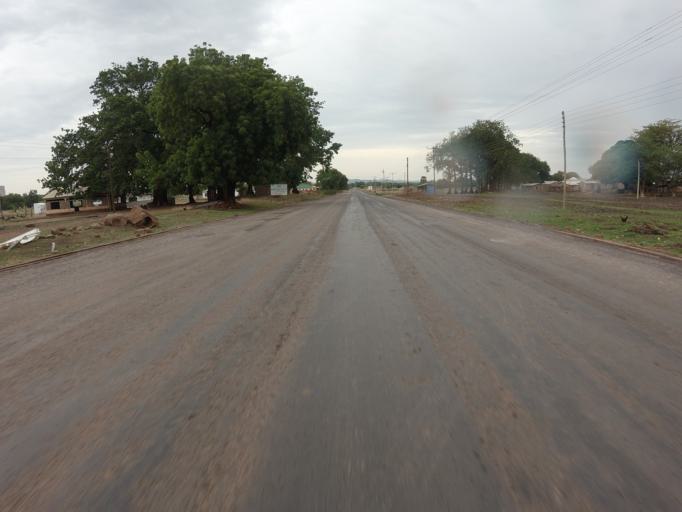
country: GH
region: Upper East
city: Bolgatanga
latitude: 10.8605
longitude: -0.6634
